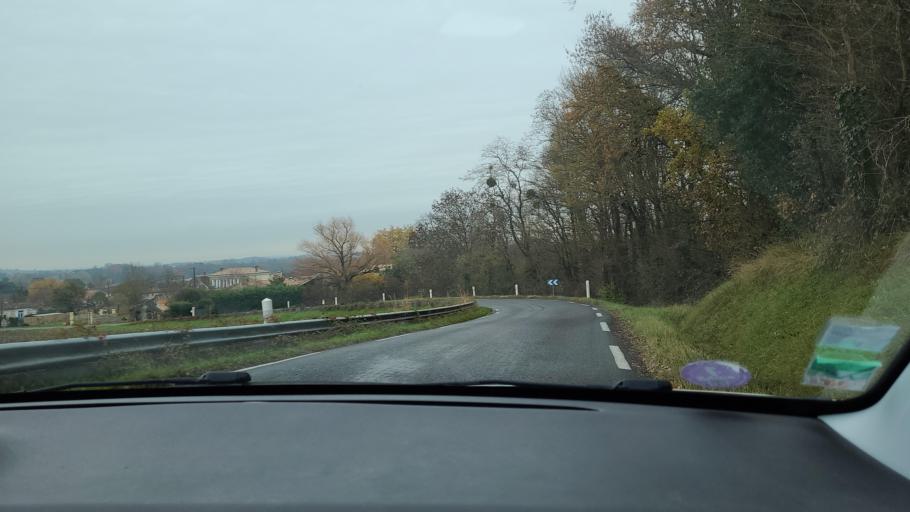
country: FR
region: Aquitaine
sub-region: Departement de la Gironde
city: Berson
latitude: 45.0852
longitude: -0.5493
